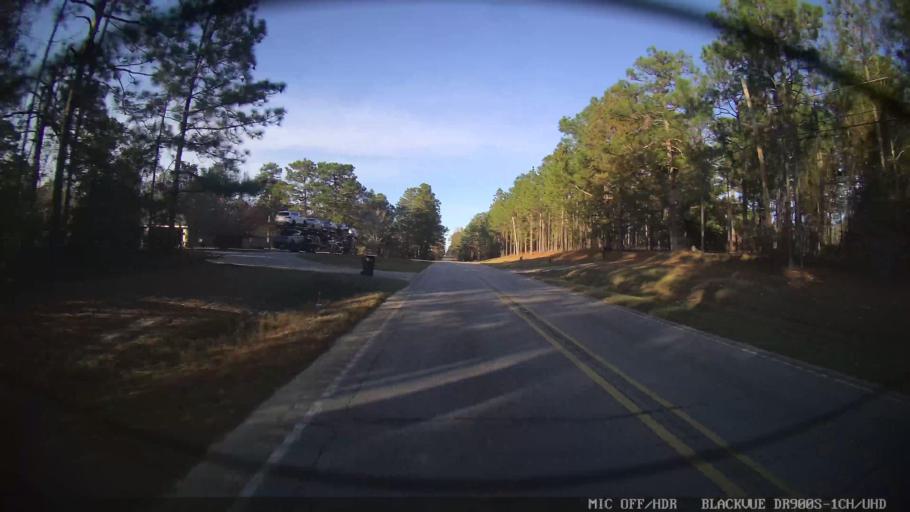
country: US
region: Mississippi
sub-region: Lamar County
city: Purvis
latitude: 31.1197
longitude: -89.4089
